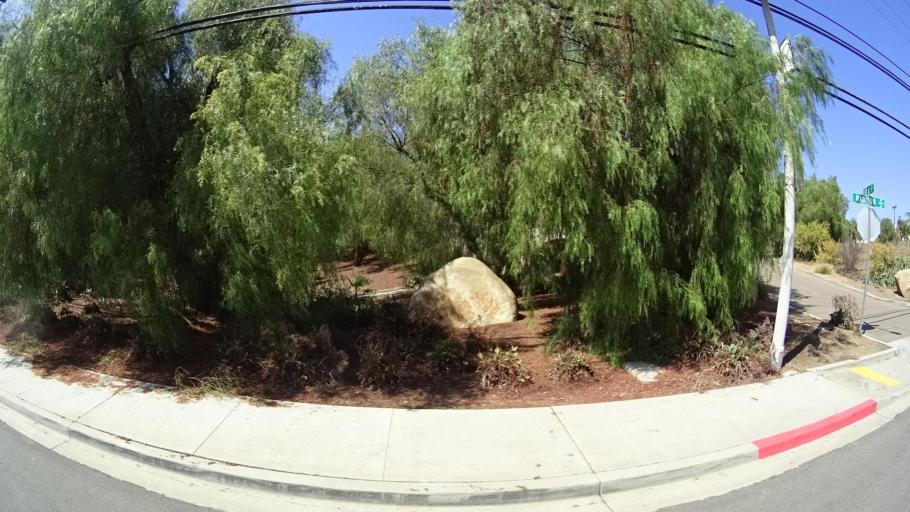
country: US
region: California
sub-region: San Diego County
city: Granite Hills
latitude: 32.8031
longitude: -116.9022
